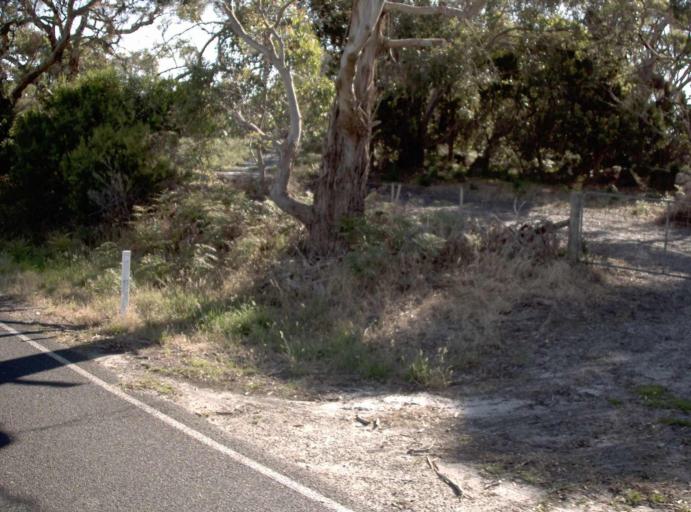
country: AU
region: Victoria
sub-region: Latrobe
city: Morwell
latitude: -38.7003
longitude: 146.3988
